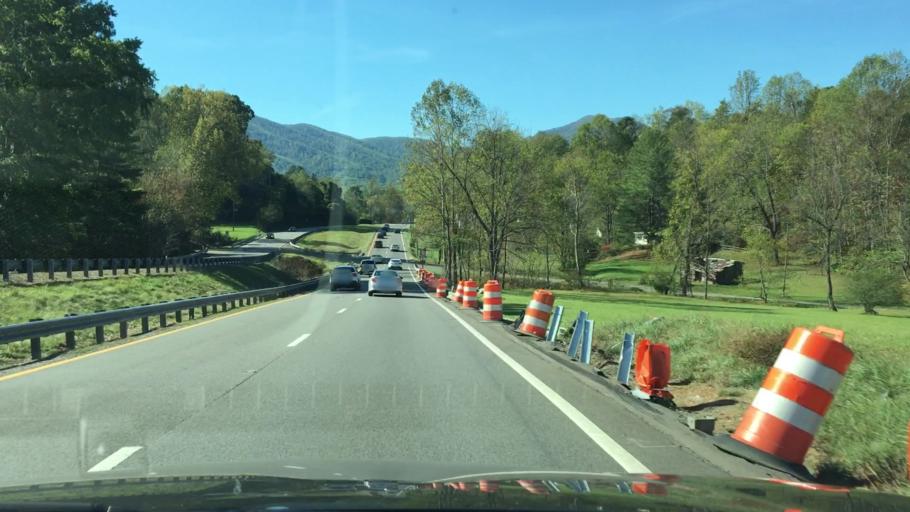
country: US
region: Virginia
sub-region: Roanoke County
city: Narrows
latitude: 37.1477
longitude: -79.9652
